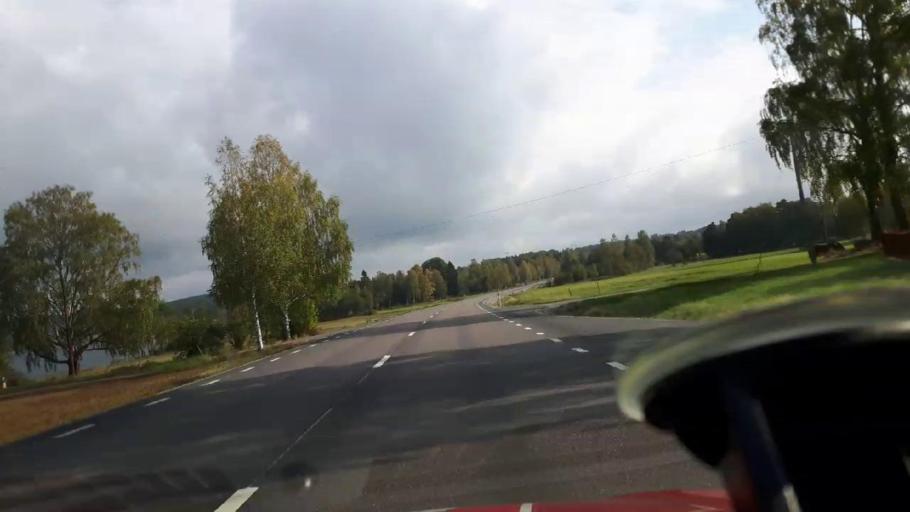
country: SE
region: Gaevleborg
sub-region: Bollnas Kommun
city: Kilafors
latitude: 61.1719
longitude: 16.8073
